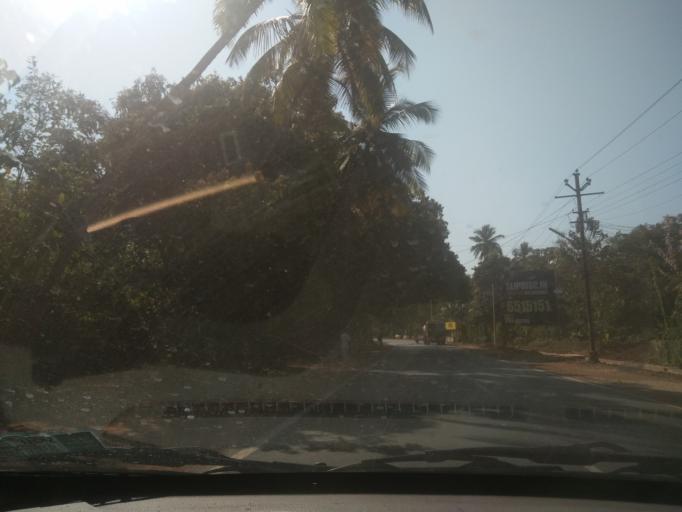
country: IN
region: Goa
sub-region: South Goa
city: Chicalim
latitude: 15.3978
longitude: 73.8704
